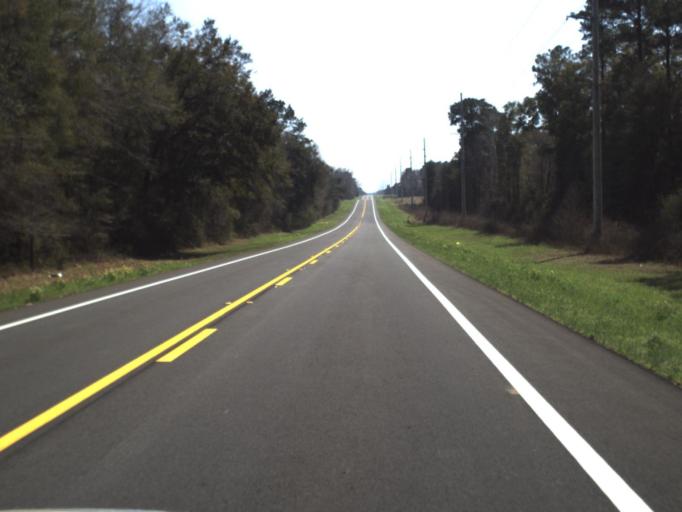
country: US
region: Florida
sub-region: Jackson County
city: Sneads
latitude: 30.8175
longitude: -85.0451
